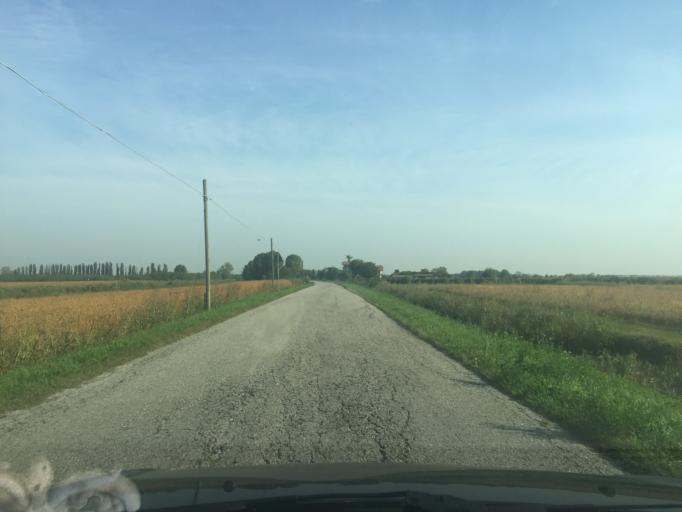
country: IT
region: Veneto
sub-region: Provincia di Venezia
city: Passarella
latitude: 45.6251
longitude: 12.6460
